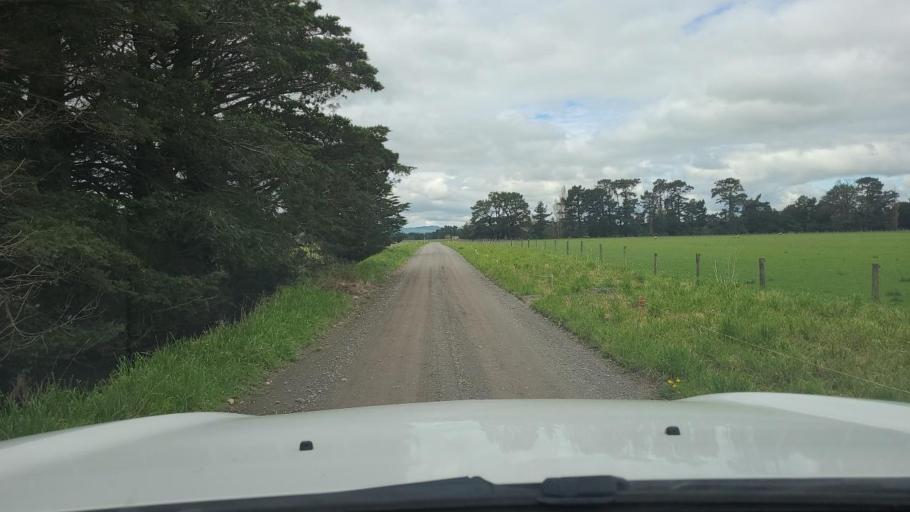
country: NZ
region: Wellington
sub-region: South Wairarapa District
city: Waipawa
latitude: -41.1482
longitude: 175.3871
